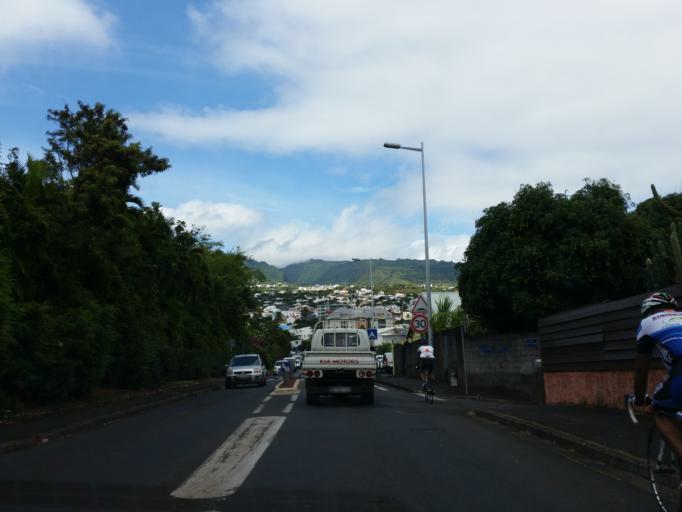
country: RE
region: Reunion
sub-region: Reunion
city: Saint-Denis
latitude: -20.9049
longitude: 55.4907
